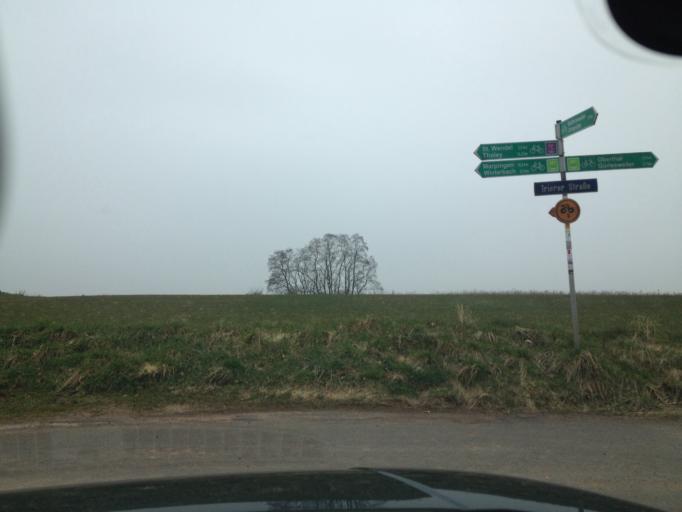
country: DE
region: Saarland
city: Sankt Wendel
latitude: 49.4908
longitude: 7.1577
